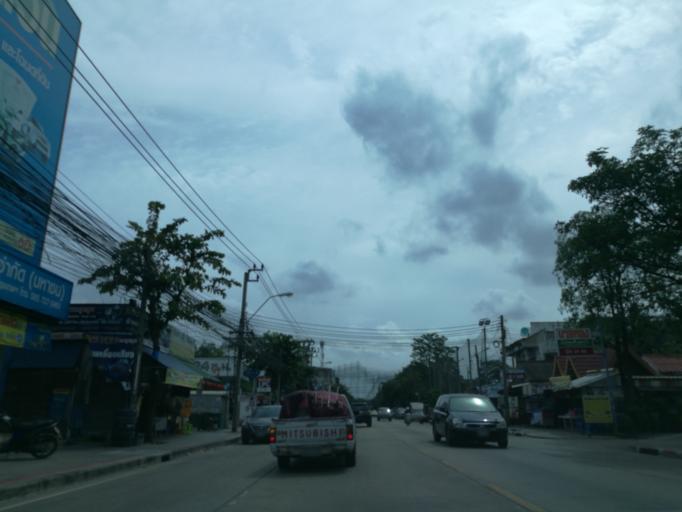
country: TH
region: Bangkok
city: Khan Na Yao
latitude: 13.8450
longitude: 100.6472
